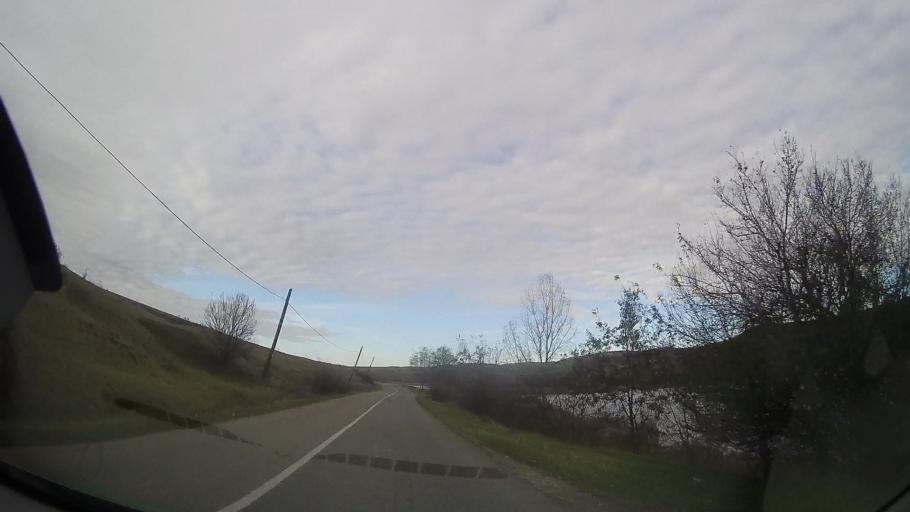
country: RO
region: Cluj
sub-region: Comuna Geaca
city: Geaca
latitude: 46.8428
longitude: 24.1236
